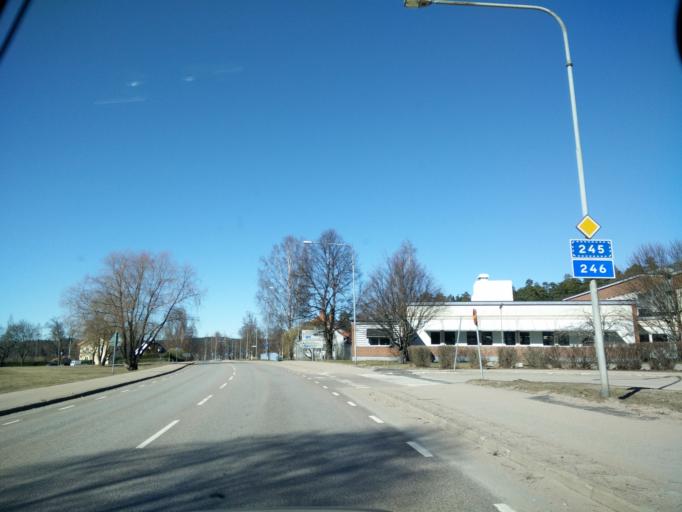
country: SE
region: Vaermland
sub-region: Hagfors Kommun
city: Hagfors
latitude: 60.0360
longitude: 13.7059
